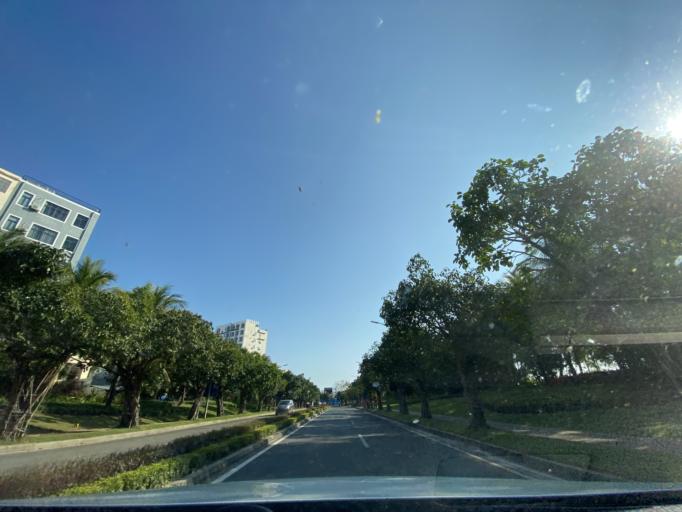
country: CN
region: Hainan
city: Xincun
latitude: 18.4167
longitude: 109.9610
